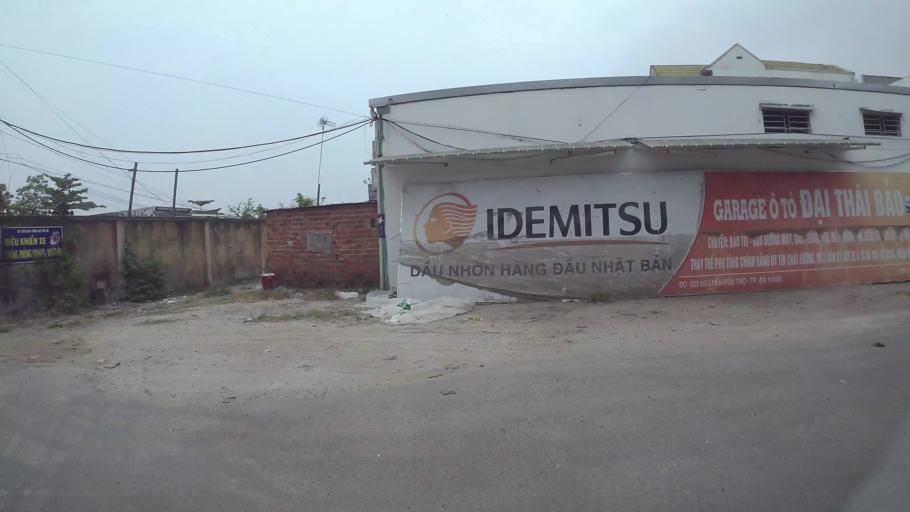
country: VN
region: Da Nang
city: Cam Le
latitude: 16.0286
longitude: 108.2083
